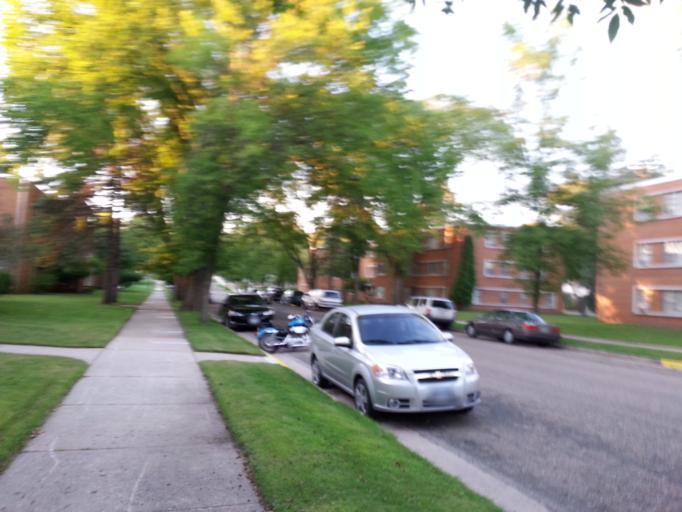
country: US
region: Minnesota
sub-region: Olmsted County
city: Rochester
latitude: 44.0374
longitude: -92.4583
